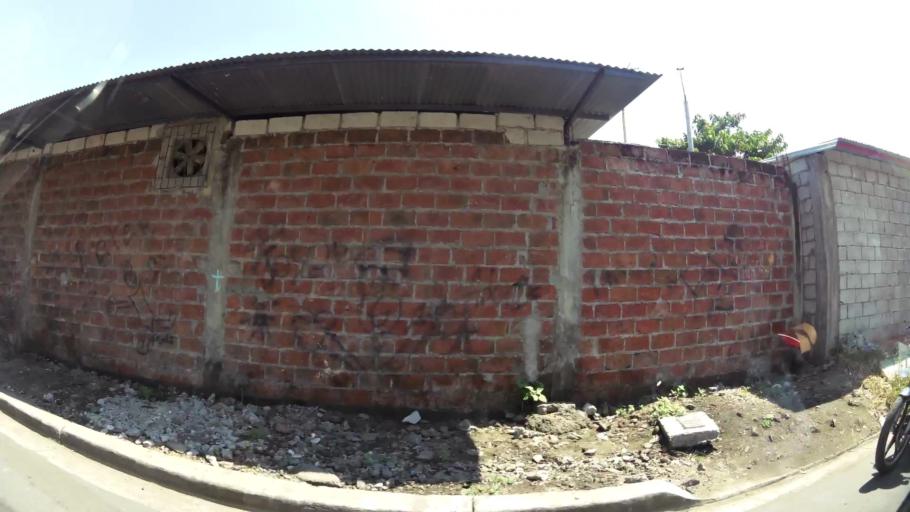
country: EC
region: Guayas
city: Guayaquil
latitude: -2.2371
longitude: -79.9164
